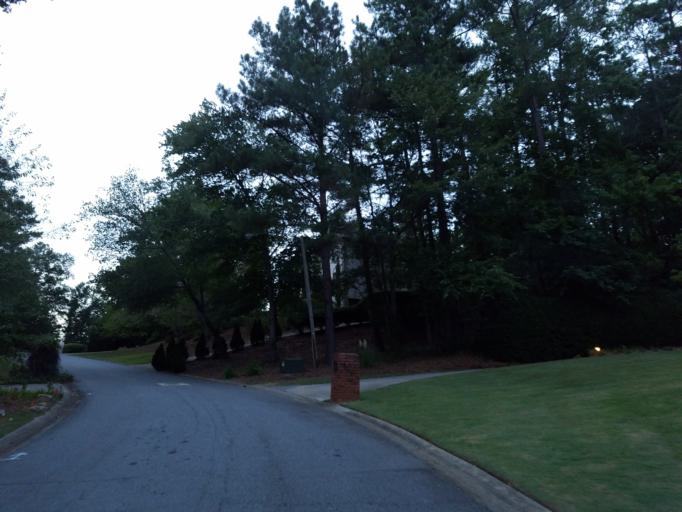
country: US
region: Georgia
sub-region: Fulton County
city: Sandy Springs
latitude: 33.9521
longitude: -84.4387
